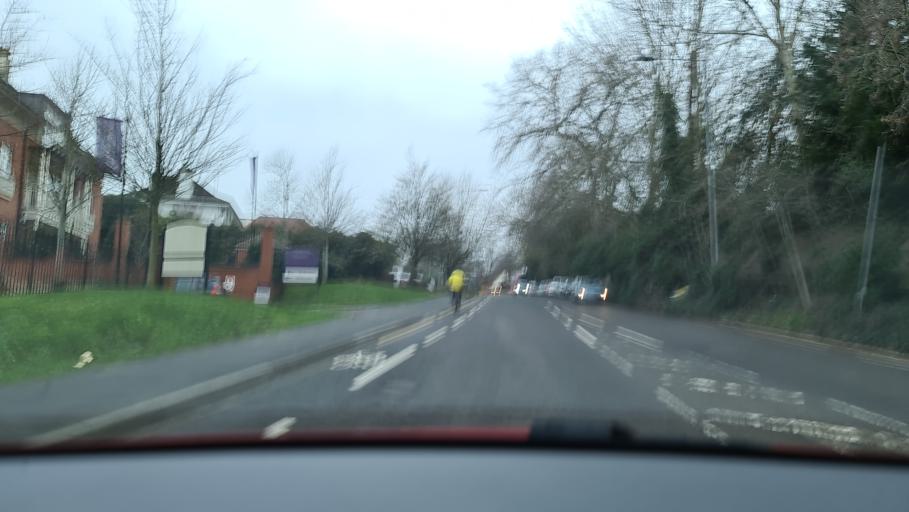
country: GB
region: England
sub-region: Greater London
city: New Malden
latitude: 51.4159
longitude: -0.2525
